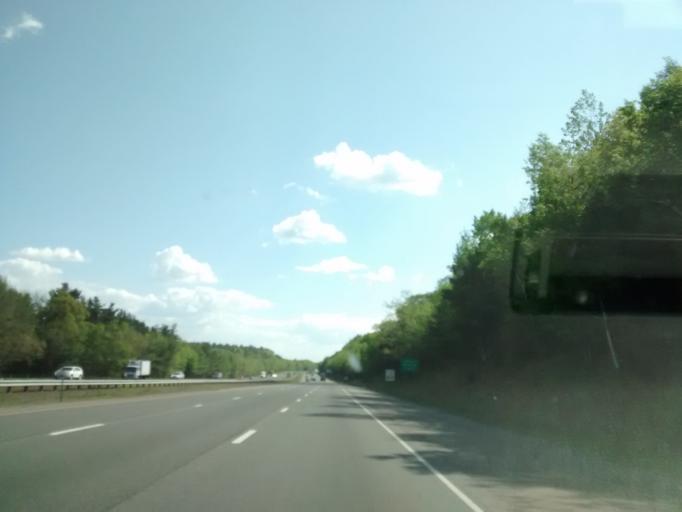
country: US
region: Massachusetts
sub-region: Hampden County
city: Holland
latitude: 42.0066
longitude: -72.1618
